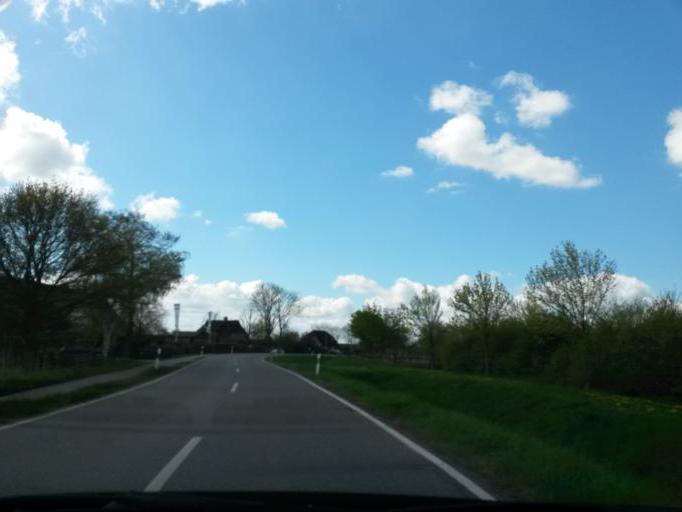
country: DE
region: Schleswig-Holstein
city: Neuendeich
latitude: 53.6754
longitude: 9.6293
